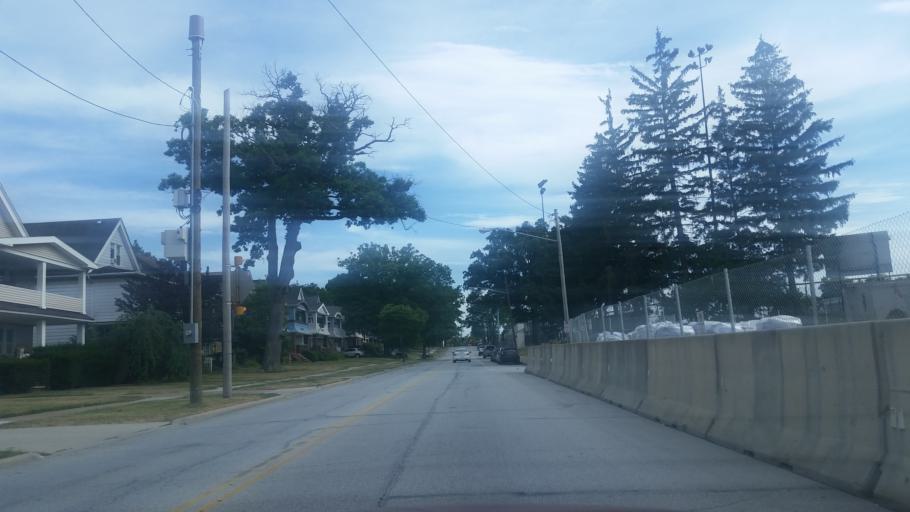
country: US
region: Ohio
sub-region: Cuyahoga County
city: Lakewood
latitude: 41.4805
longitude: -81.7896
